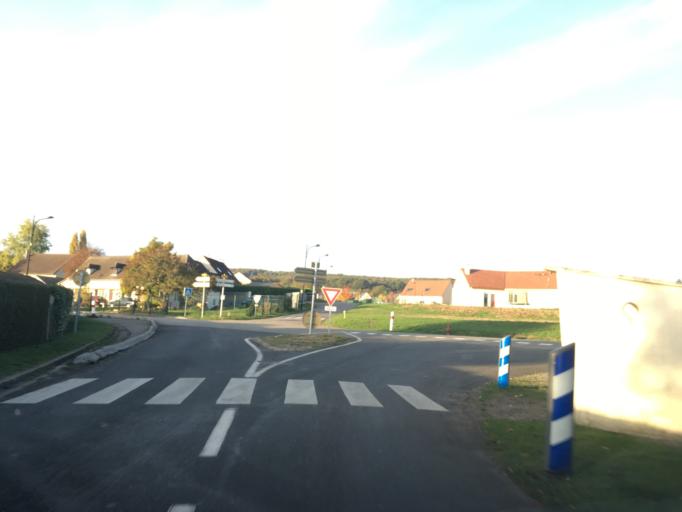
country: FR
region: Haute-Normandie
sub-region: Departement de l'Eure
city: Heudreville-sur-Eure
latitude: 49.1264
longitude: 1.2159
